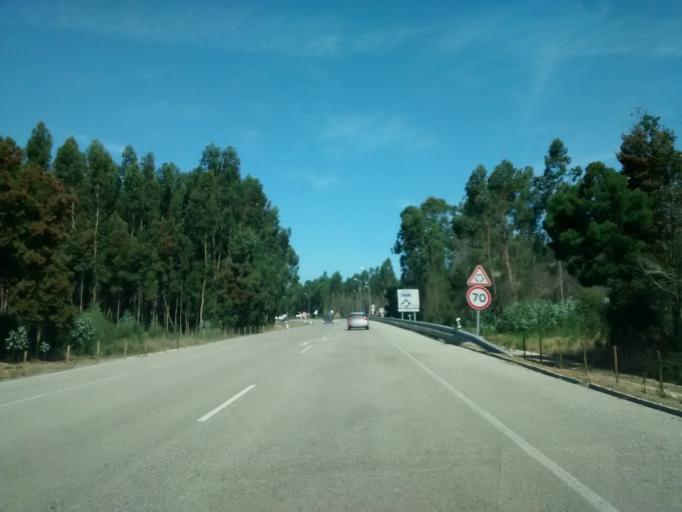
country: PT
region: Coimbra
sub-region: Mira
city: Mira
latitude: 40.4459
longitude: -8.7412
